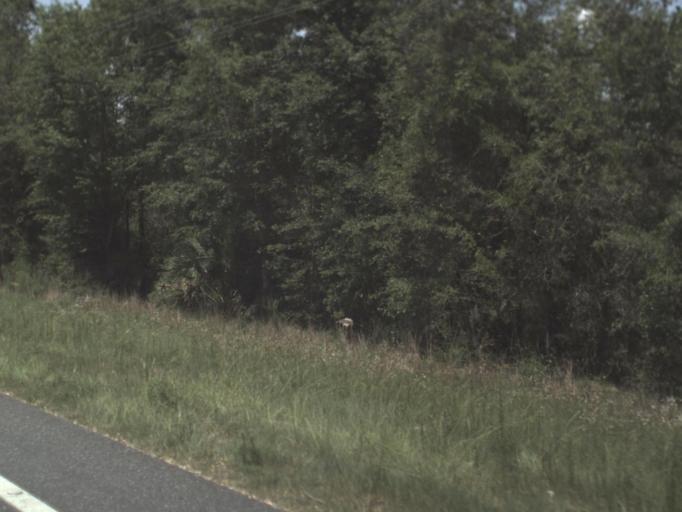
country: US
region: Florida
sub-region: Gilchrist County
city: Trenton
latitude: 29.8024
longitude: -82.8669
